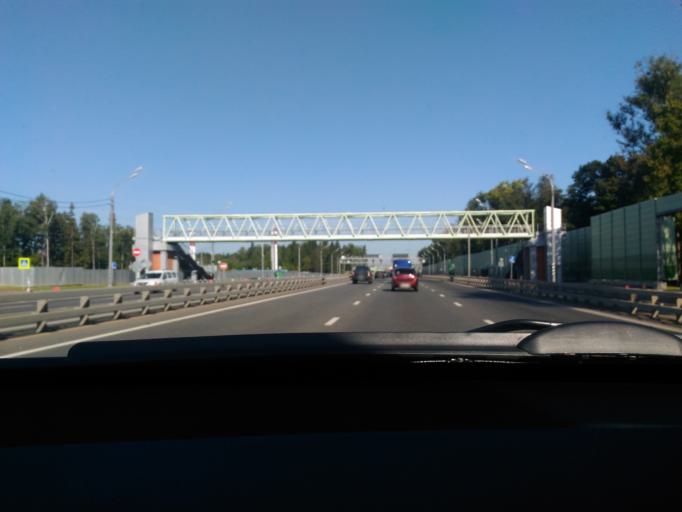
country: RU
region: Moskovskaya
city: Yermolino
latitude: 56.1320
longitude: 37.5057
